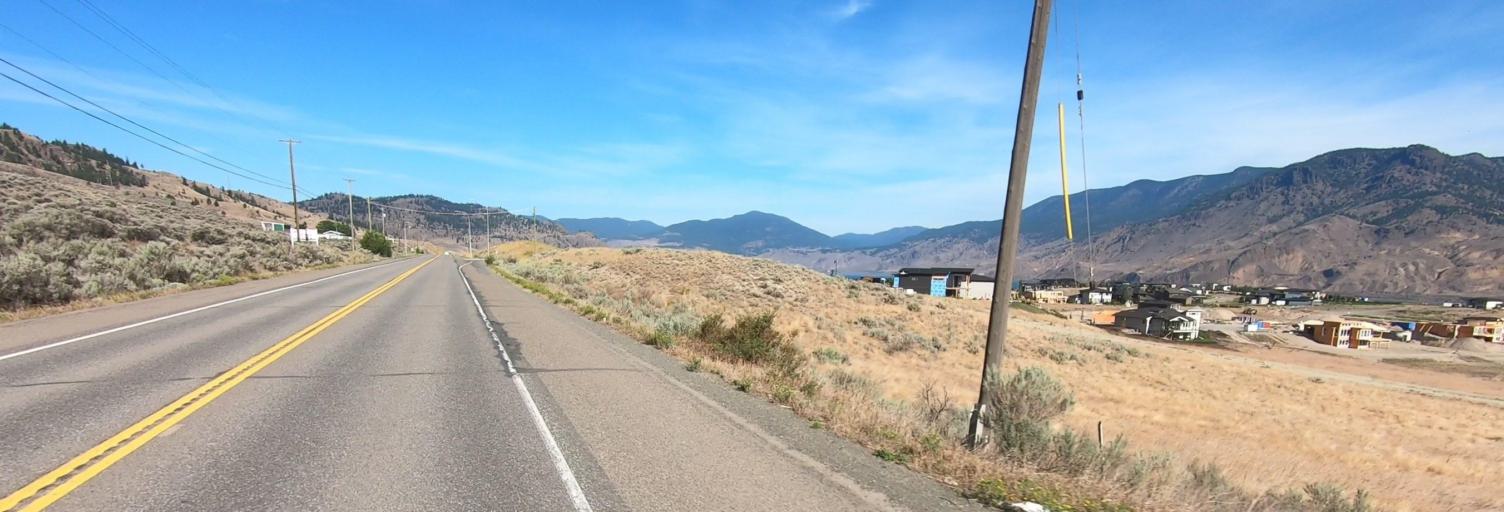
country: CA
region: British Columbia
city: Logan Lake
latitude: 50.7260
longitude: -120.6739
